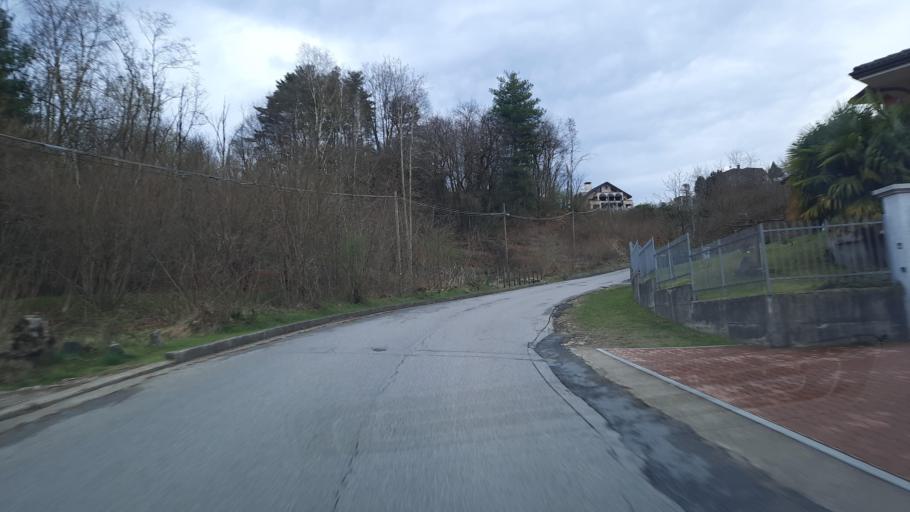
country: IT
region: Piedmont
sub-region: Provincia di Novara
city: San Maurizio D'Opaglio
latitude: 45.7801
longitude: 8.3929
